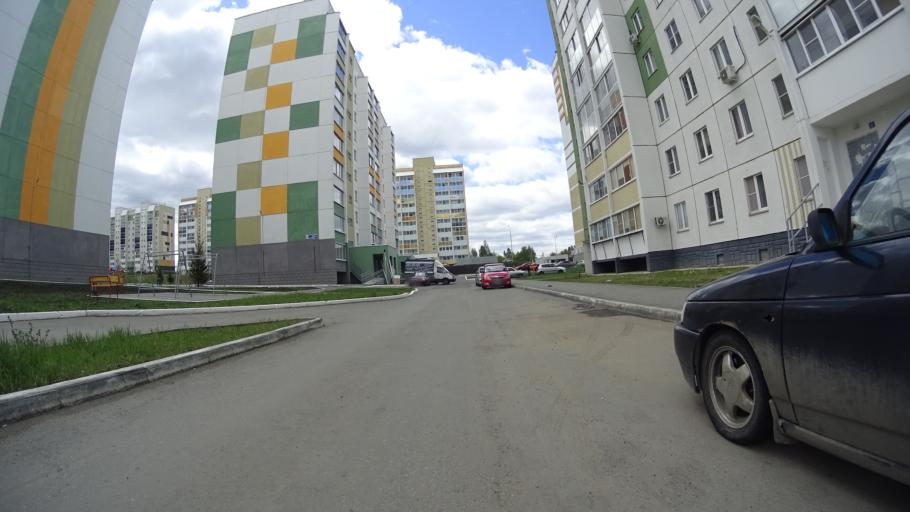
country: RU
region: Chelyabinsk
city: Roshchino
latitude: 55.1742
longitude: 61.2588
